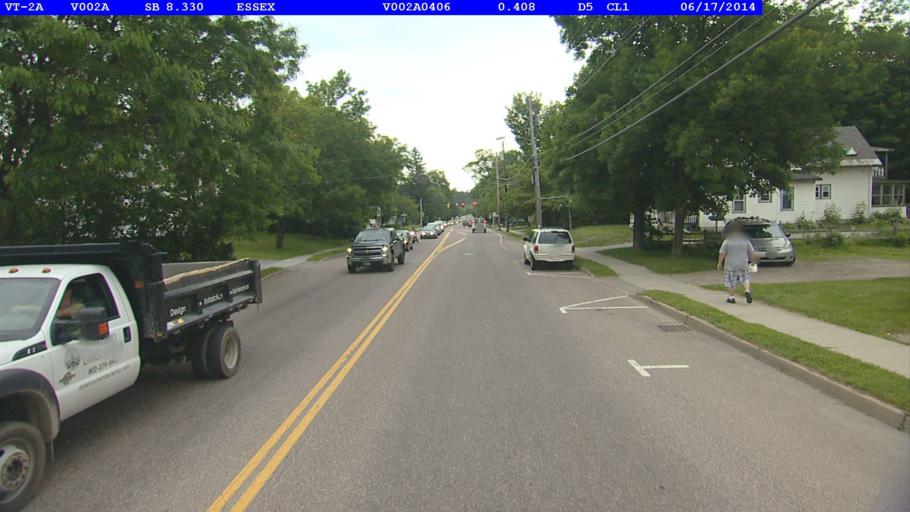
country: US
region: Vermont
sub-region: Chittenden County
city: Essex Junction
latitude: 44.4869
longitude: -73.1133
